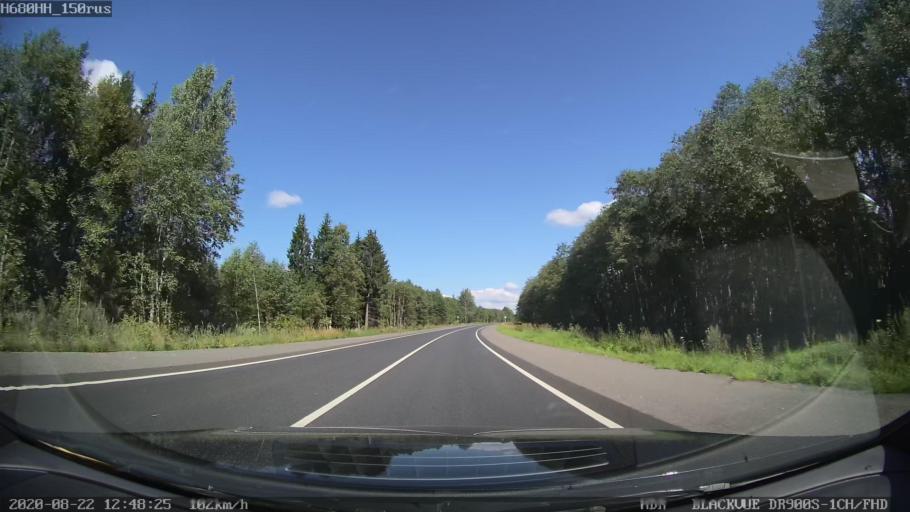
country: RU
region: Tverskaya
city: Rameshki
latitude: 57.4395
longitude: 36.1842
